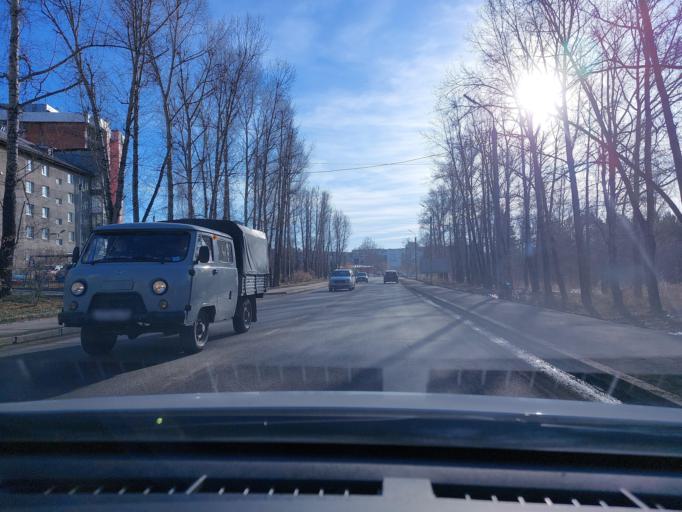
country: RU
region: Irkutsk
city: Dzerzhinsk
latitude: 52.2553
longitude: 104.3520
